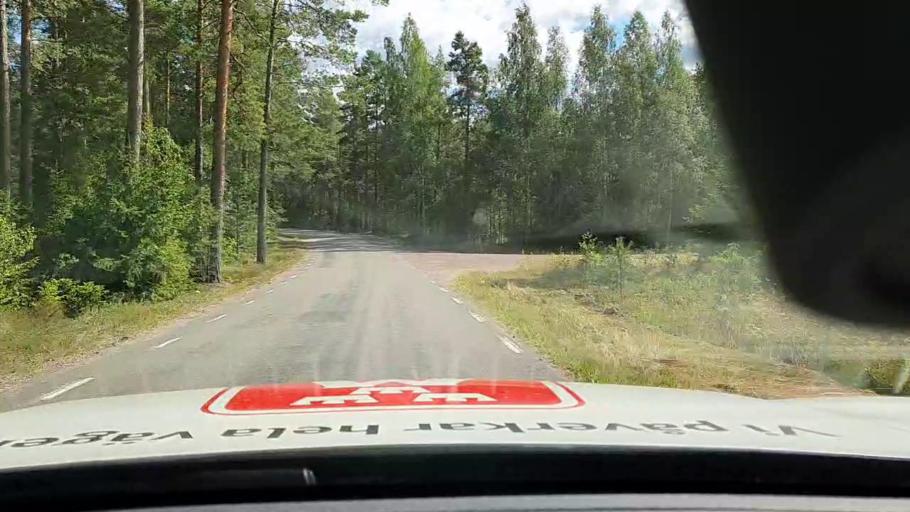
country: SE
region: Vaestra Goetaland
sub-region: Karlsborgs Kommun
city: Molltorp
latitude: 58.6044
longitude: 14.3685
